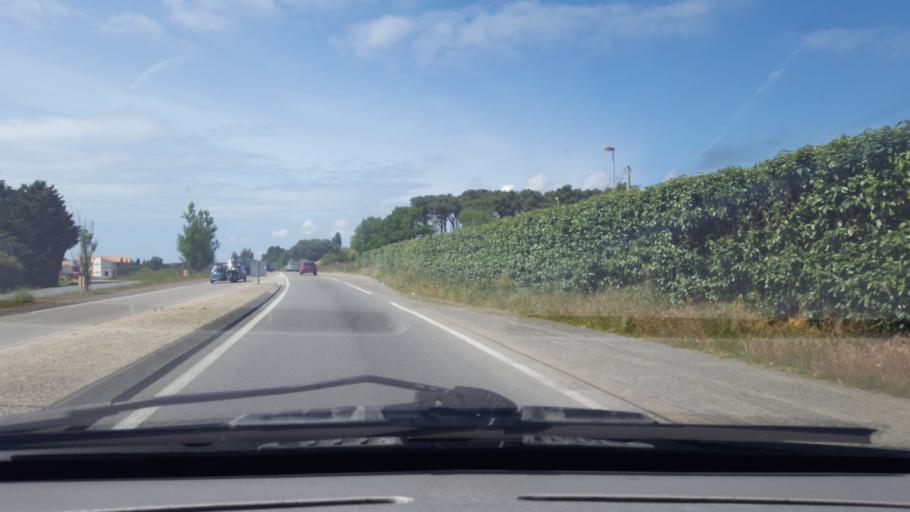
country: FR
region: Pays de la Loire
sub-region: Departement de la Loire-Atlantique
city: Bourgneuf-en-Retz
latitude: 47.0483
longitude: -1.9590
